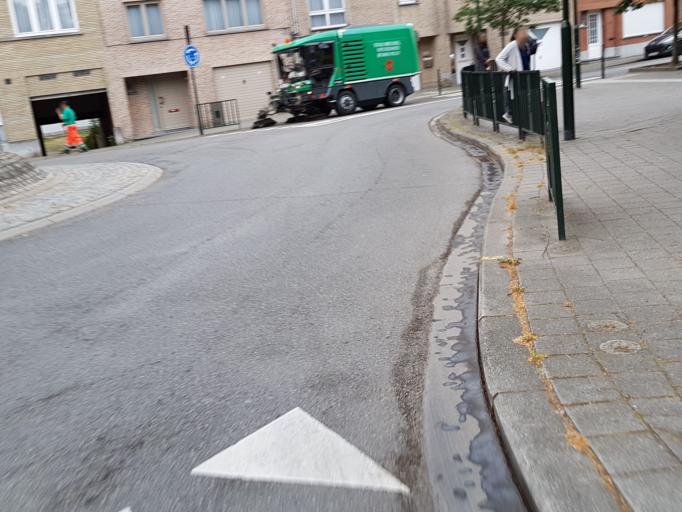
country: BE
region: Flanders
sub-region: Provincie Vlaams-Brabant
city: Grimbergen
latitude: 50.8957
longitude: 4.3715
